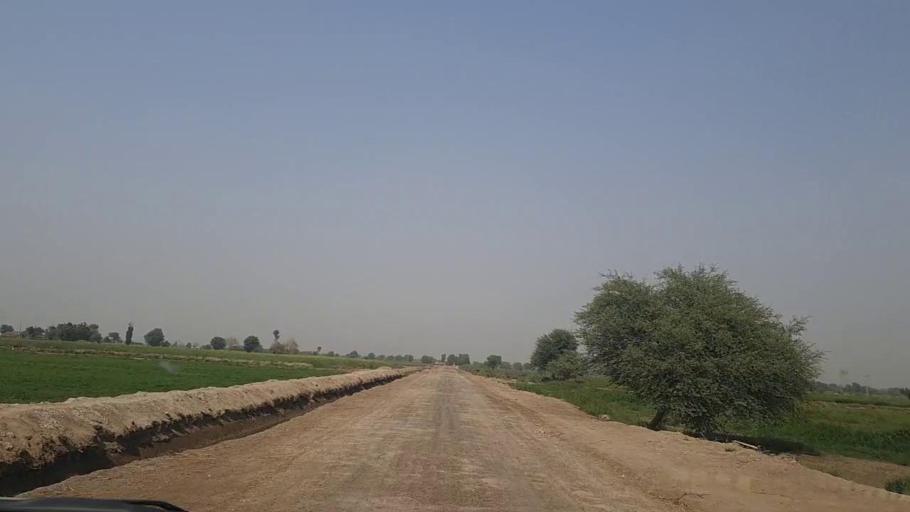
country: PK
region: Sindh
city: Mirpur Khas
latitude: 25.6171
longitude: 69.2009
